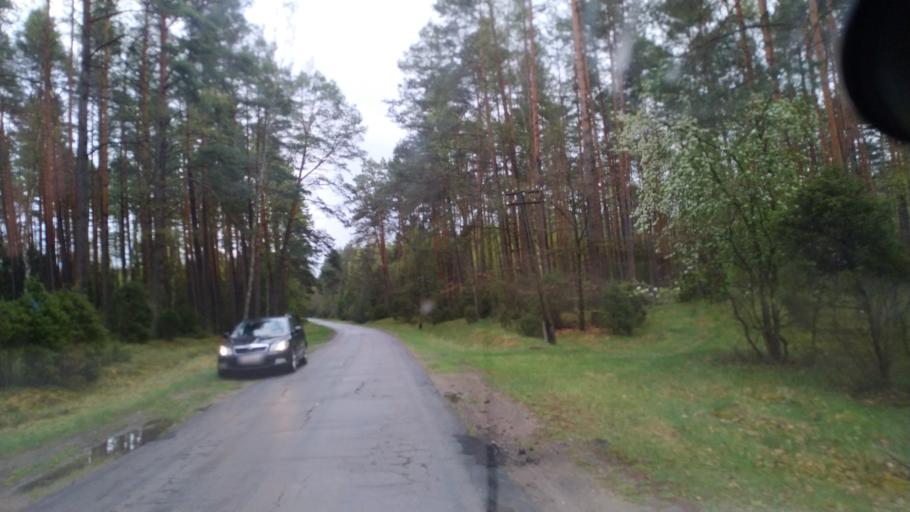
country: PL
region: Pomeranian Voivodeship
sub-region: Powiat starogardzki
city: Osiek
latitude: 53.6641
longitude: 18.4817
